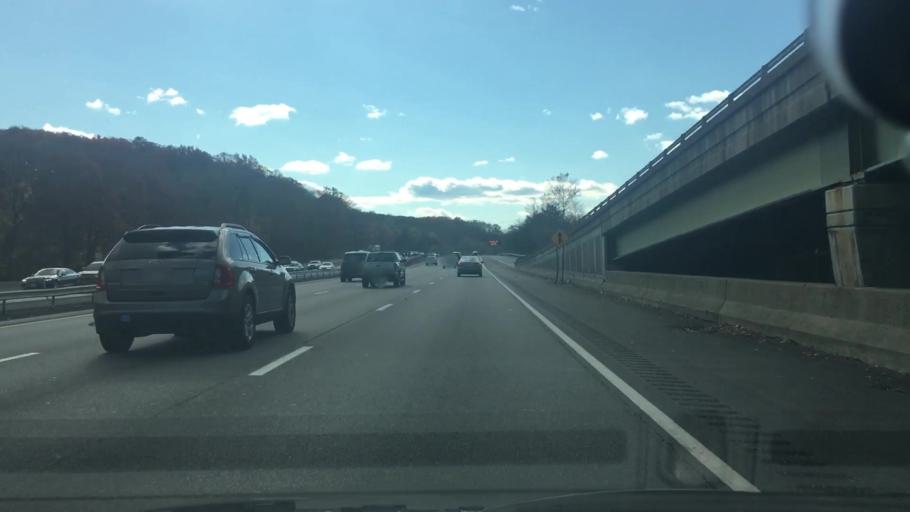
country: US
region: New York
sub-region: Westchester County
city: Goldens Bridge
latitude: 41.2938
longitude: -73.6774
